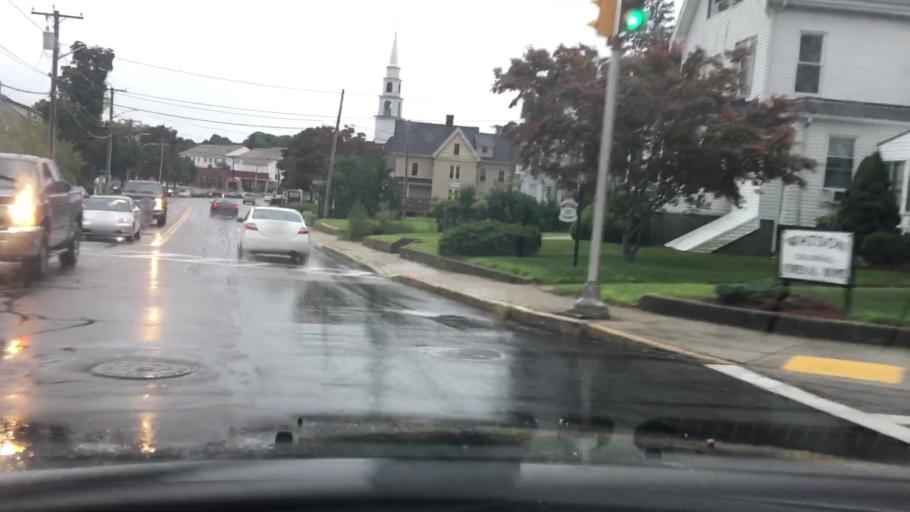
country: US
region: Massachusetts
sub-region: Worcester County
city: Milford
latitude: 42.1407
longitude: -71.5228
